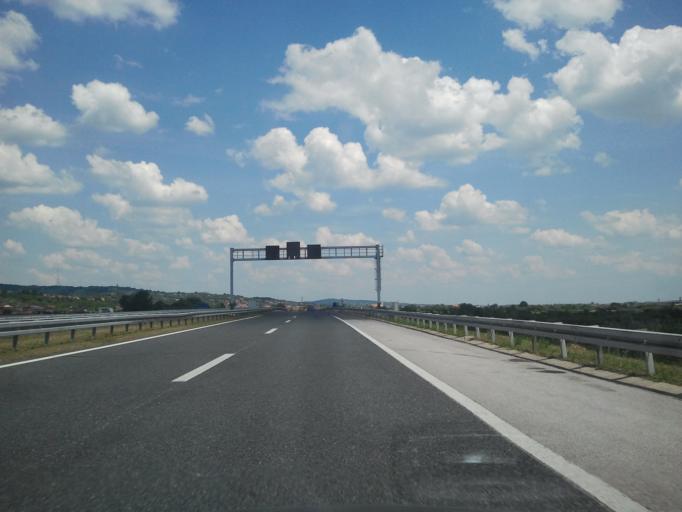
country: HR
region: Brodsko-Posavska
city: Slobodnica
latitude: 45.1720
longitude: 17.9497
